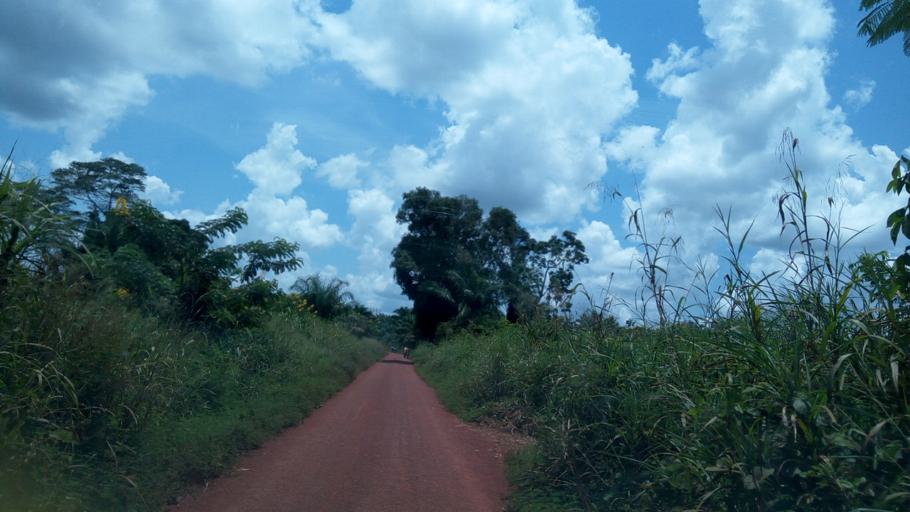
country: CD
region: Equateur
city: Libenge
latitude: 3.7520
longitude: 19.0602
